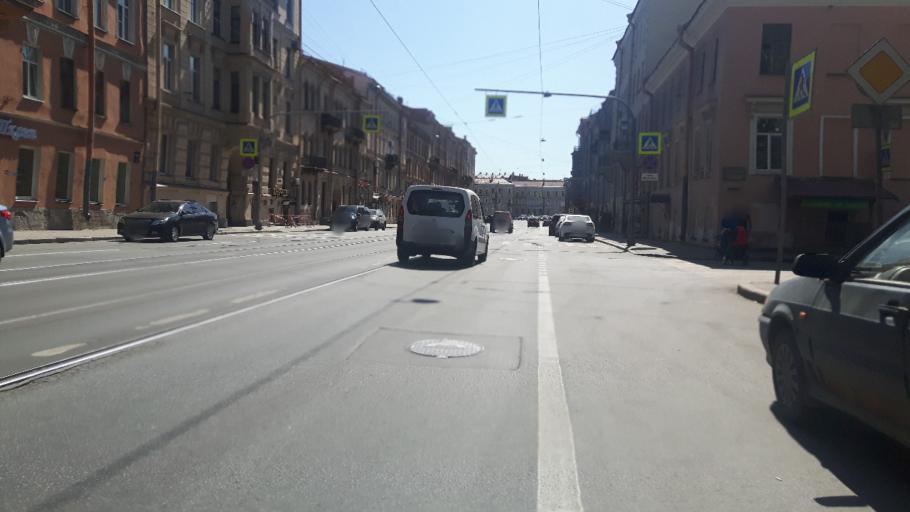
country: RU
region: St.-Petersburg
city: Admiralteisky
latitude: 59.9190
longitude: 30.2956
